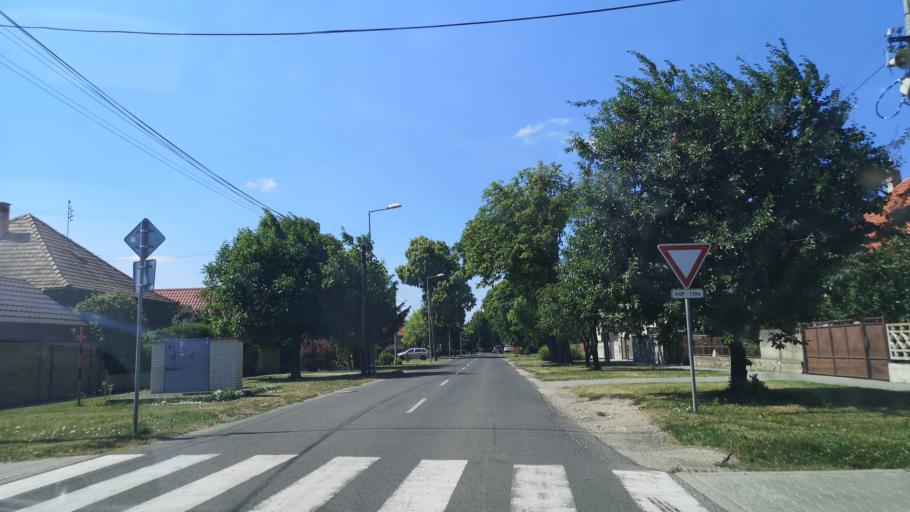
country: SK
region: Trnavsky
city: Samorin
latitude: 48.0525
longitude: 17.4594
